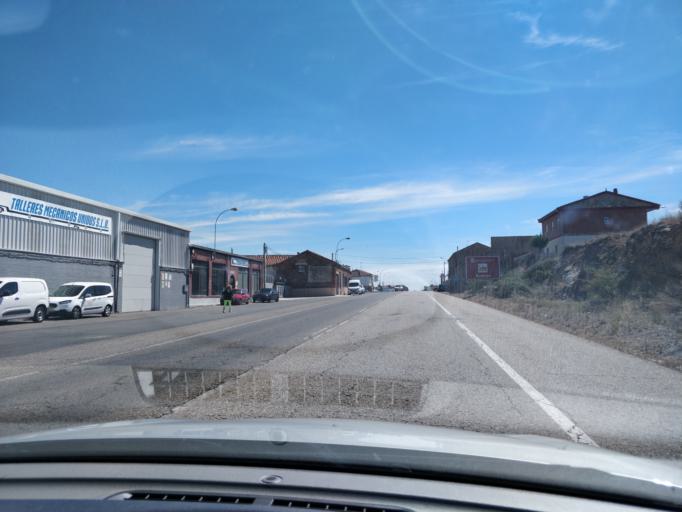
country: ES
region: Castille and Leon
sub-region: Provincia de Leon
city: Astorga
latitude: 42.4660
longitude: -6.0756
